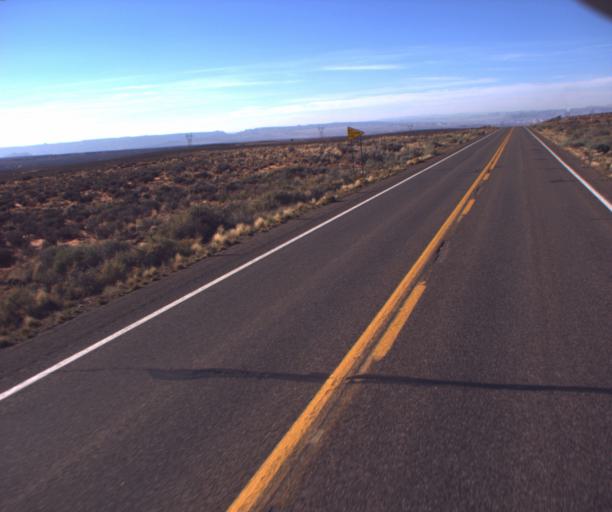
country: US
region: Arizona
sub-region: Coconino County
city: LeChee
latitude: 36.8290
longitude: -111.3114
